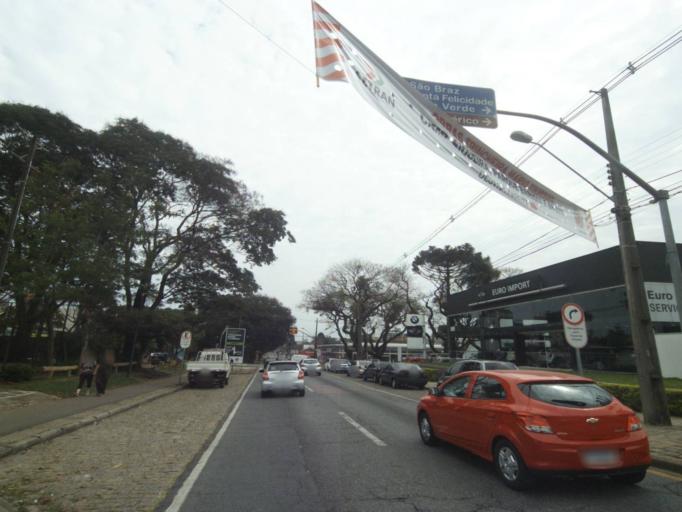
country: BR
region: Parana
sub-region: Curitiba
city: Curitiba
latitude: -25.4574
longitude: -49.3027
